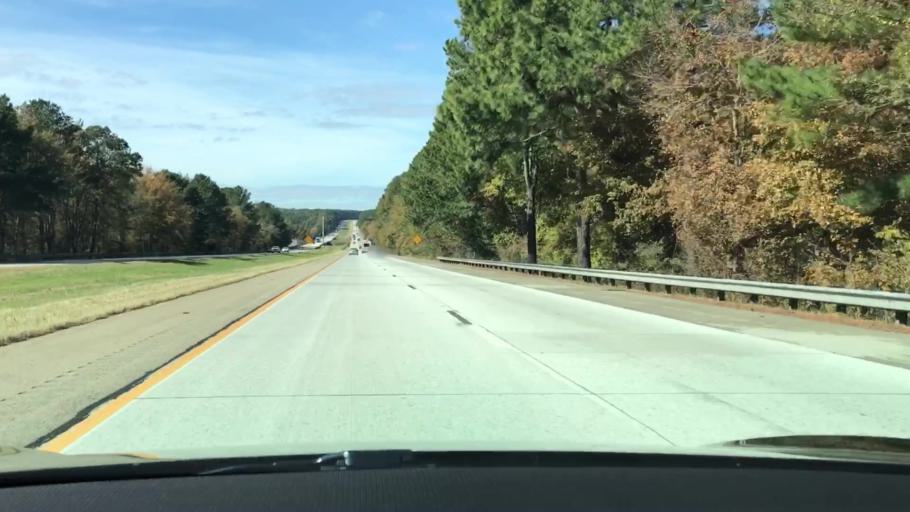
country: US
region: Georgia
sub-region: Greene County
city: Greensboro
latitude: 33.5348
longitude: -83.2634
